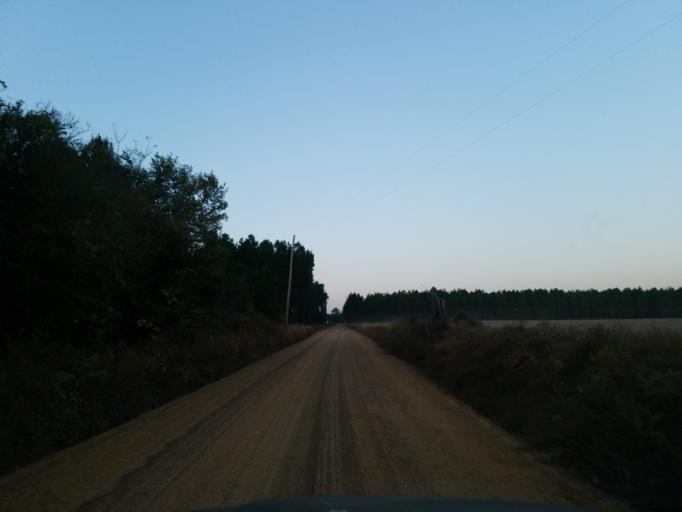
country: US
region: Georgia
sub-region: Turner County
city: Ashburn
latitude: 31.7342
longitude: -83.4844
